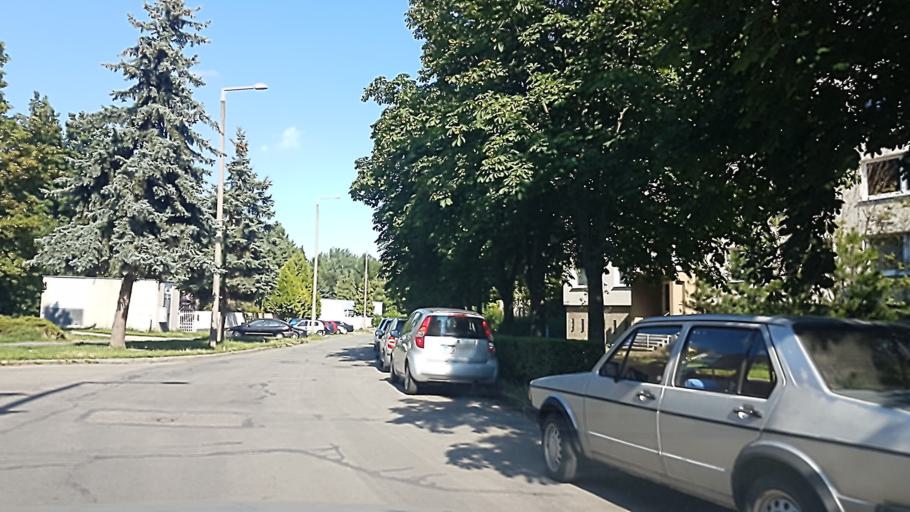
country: HU
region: Gyor-Moson-Sopron
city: Sopron
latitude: 47.6945
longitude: 16.5740
